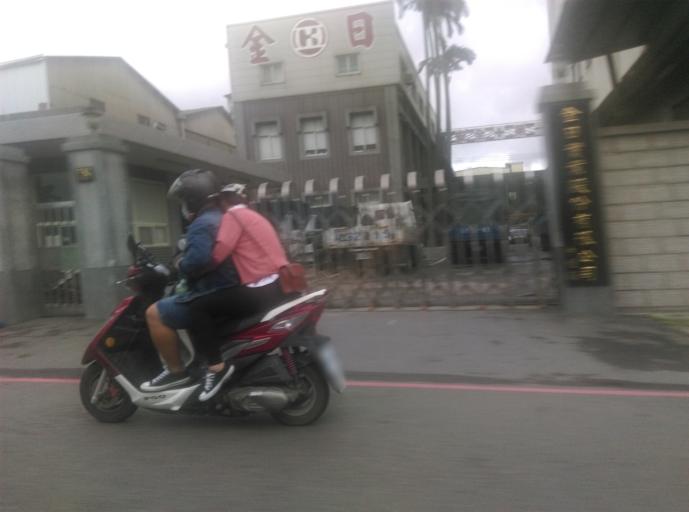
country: TW
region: Taiwan
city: Taoyuan City
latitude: 24.9880
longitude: 121.2426
